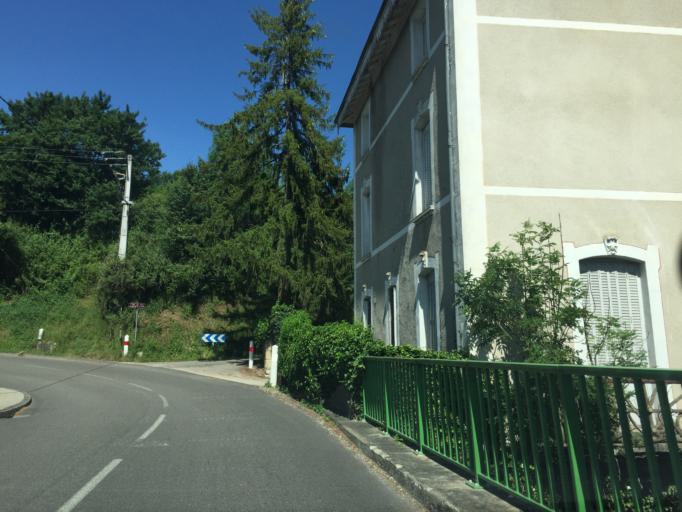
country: FR
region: Rhone-Alpes
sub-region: Departement de la Drome
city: Saint-Laurent-en-Royans
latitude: 45.0288
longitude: 5.3103
